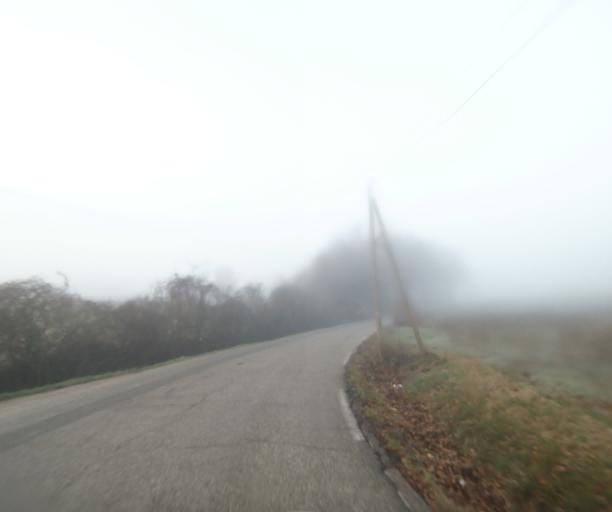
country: FR
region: Provence-Alpes-Cote d'Azur
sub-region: Departement des Bouches-du-Rhone
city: Meyreuil
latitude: 43.4853
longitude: 5.5025
